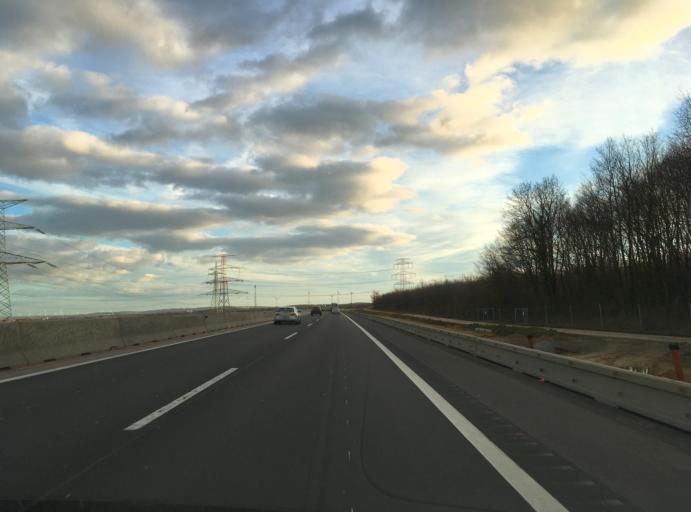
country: AT
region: Lower Austria
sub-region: Politischer Bezirk Ganserndorf
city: Orth an der Donau
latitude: 48.0798
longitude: 16.6761
